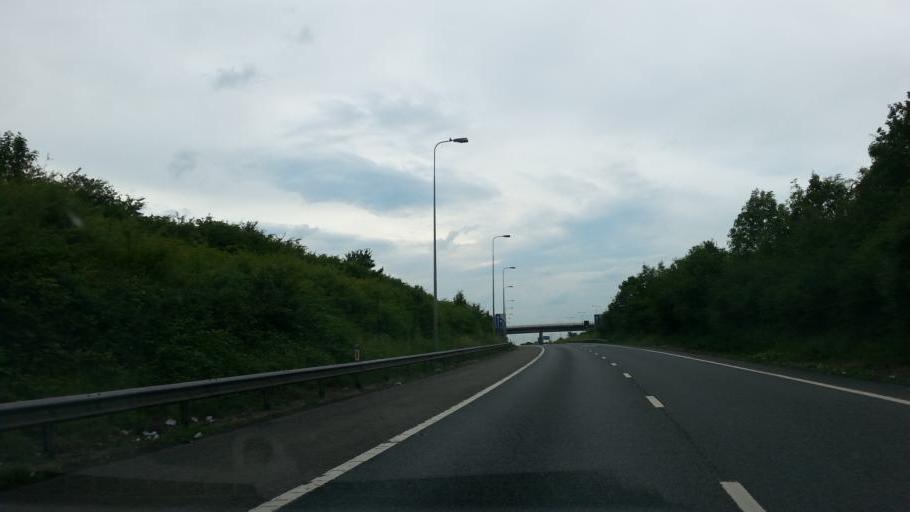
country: GB
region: England
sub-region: Worcestershire
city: Bredon
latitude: 52.0497
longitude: -2.1374
